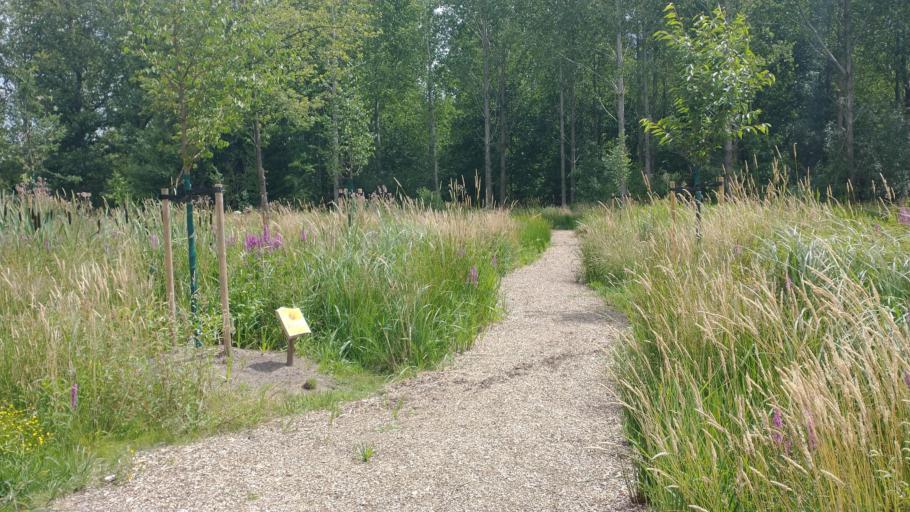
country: NL
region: Utrecht
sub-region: Gemeente Utrechtse Heuvelrug
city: Driebergen-Rijsenburg
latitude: 52.0155
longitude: 5.2828
